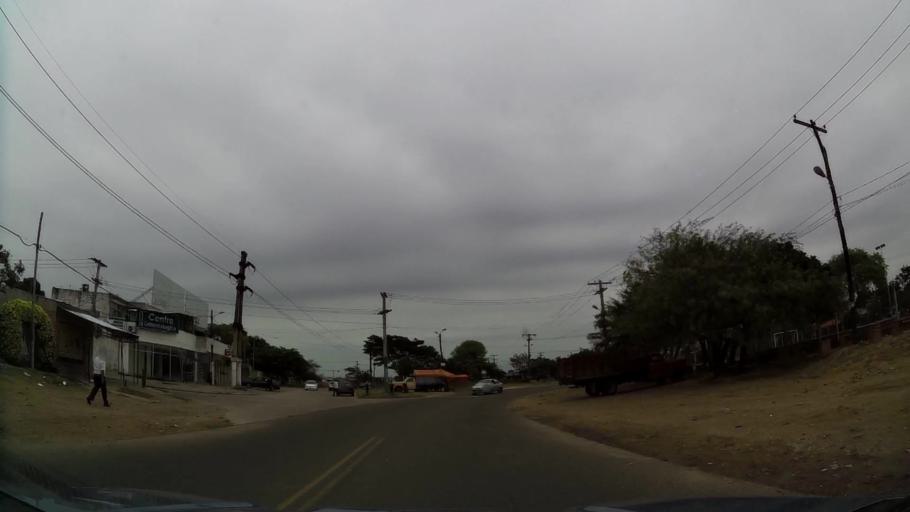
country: BO
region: Santa Cruz
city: Santa Cruz de la Sierra
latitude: -17.8073
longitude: -63.1718
